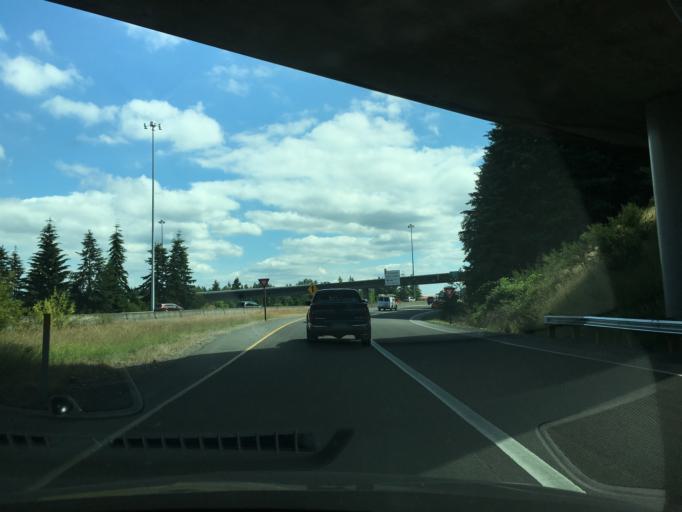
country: US
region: Washington
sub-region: Snohomish County
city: Mill Creek
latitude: 47.9167
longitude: -122.2087
